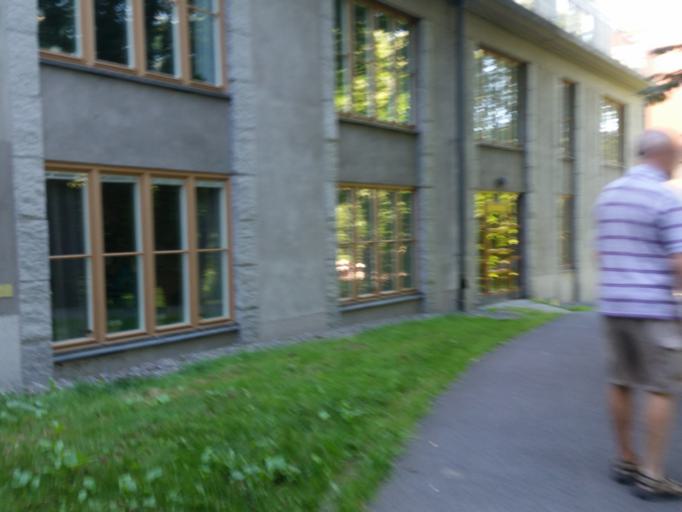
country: SE
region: Stockholm
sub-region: Stockholms Kommun
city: Stockholm
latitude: 59.3355
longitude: 18.0415
